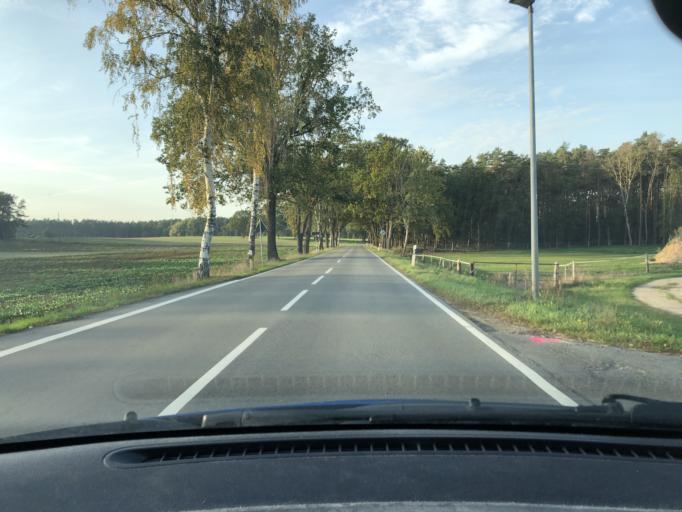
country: DE
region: Lower Saxony
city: Hitzacker
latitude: 53.1197
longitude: 11.0528
